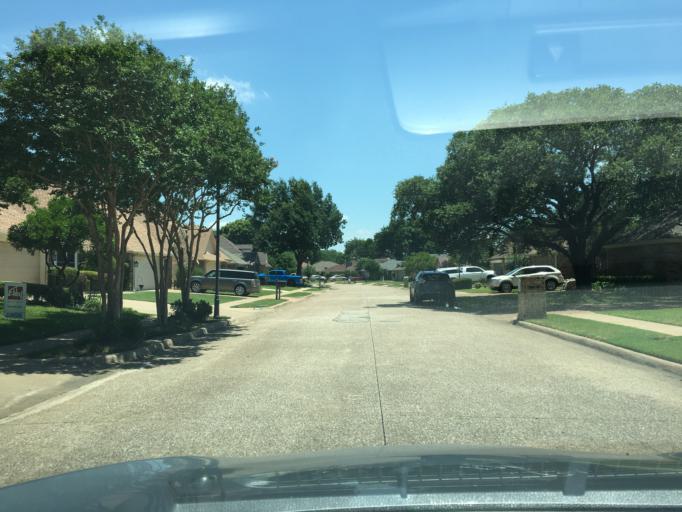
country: US
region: Texas
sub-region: Dallas County
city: Garland
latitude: 32.9426
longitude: -96.6767
